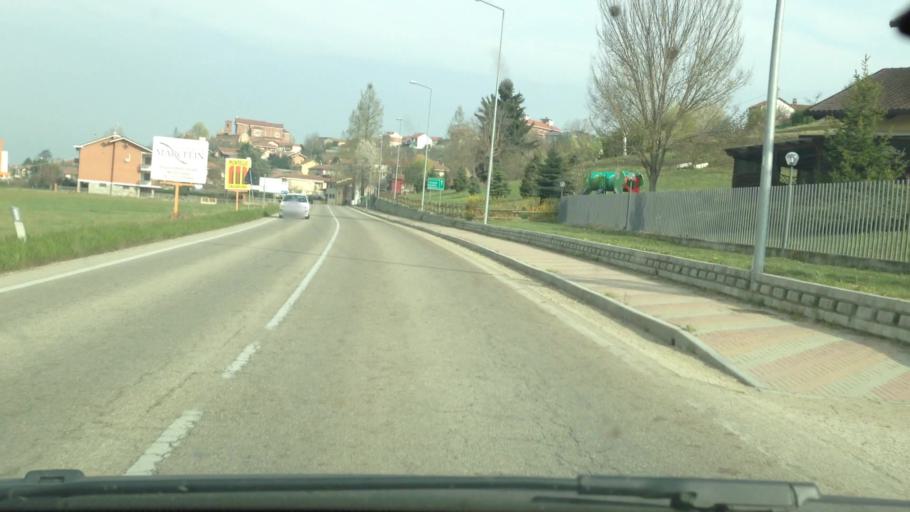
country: IT
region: Piedmont
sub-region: Provincia di Torino
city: Pralormo
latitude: 44.8550
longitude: 7.9070
